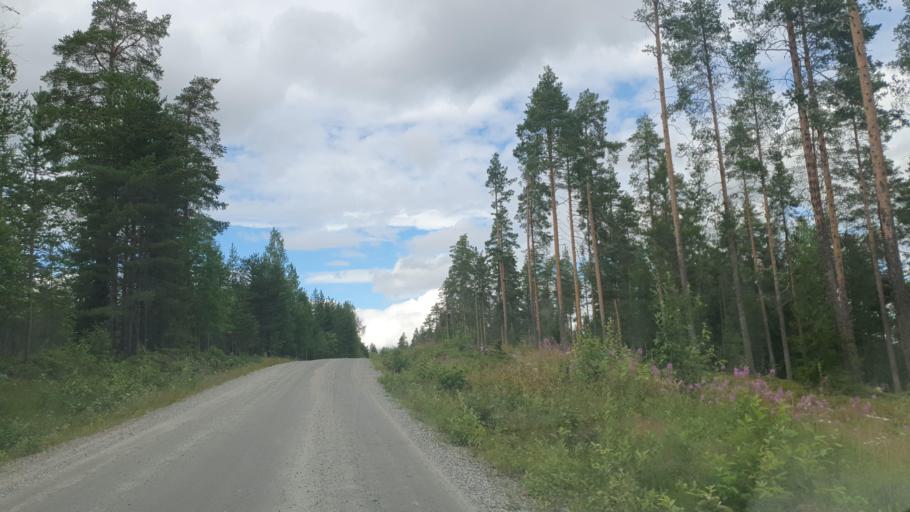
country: FI
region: Kainuu
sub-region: Kehys-Kainuu
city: Kuhmo
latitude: 64.0955
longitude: 29.4157
